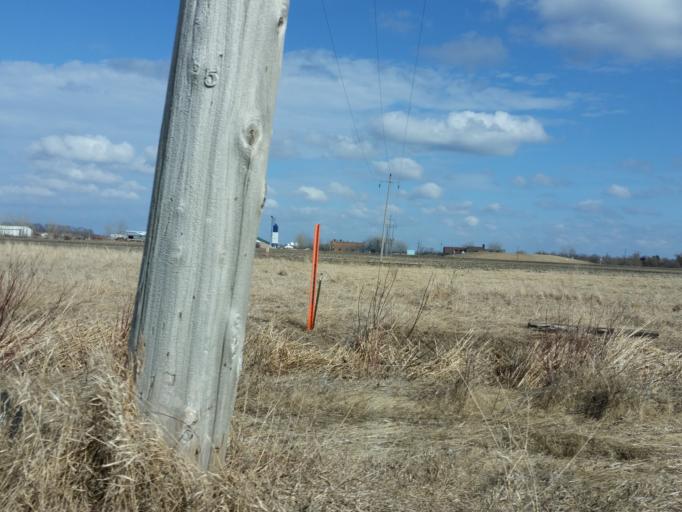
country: US
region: North Dakota
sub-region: Walsh County
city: Grafton
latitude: 48.4297
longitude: -97.4108
